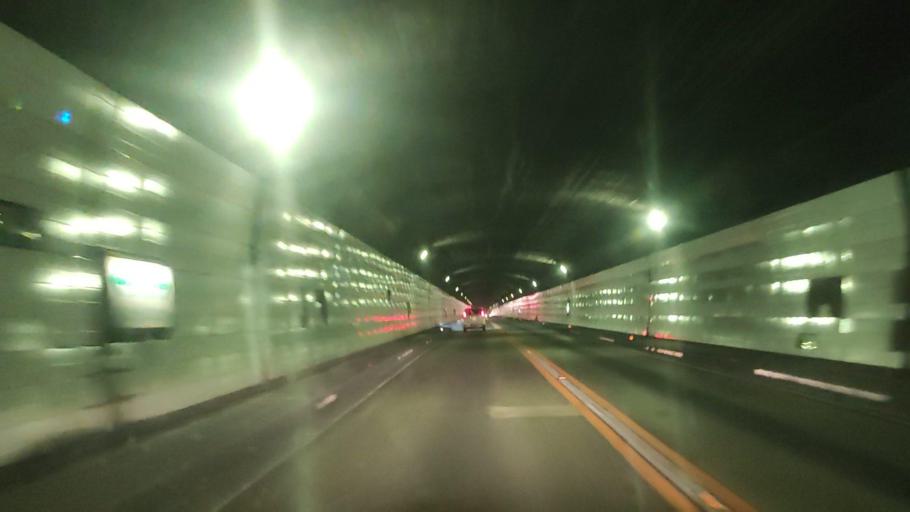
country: JP
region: Kumamoto
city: Hitoyoshi
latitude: 32.1010
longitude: 130.8043
